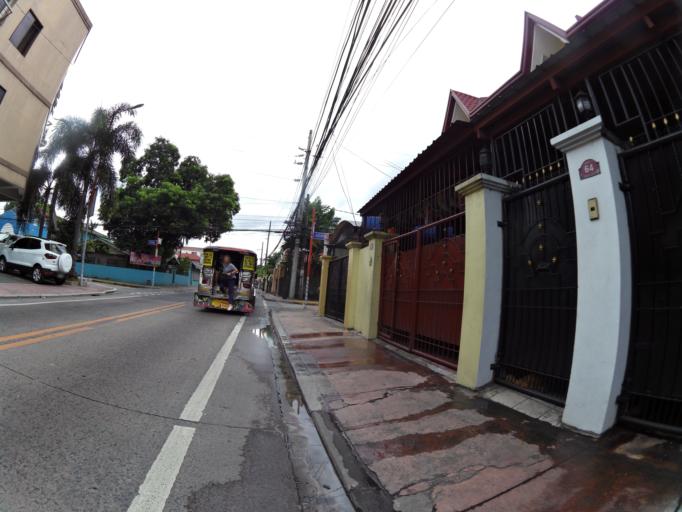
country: PH
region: Calabarzon
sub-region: Province of Rizal
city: Antipolo
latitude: 14.6410
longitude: 121.1140
